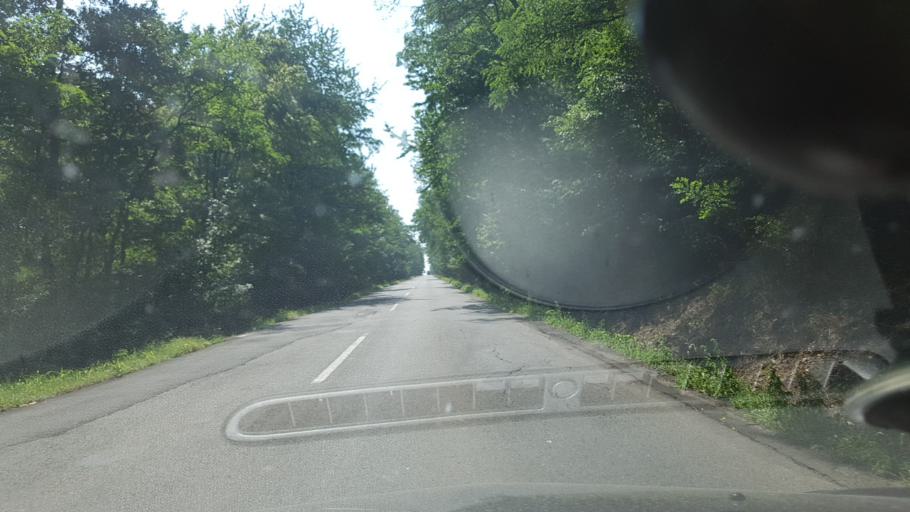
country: SK
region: Banskobystricky
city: Velky Krtis
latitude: 48.2559
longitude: 19.4254
